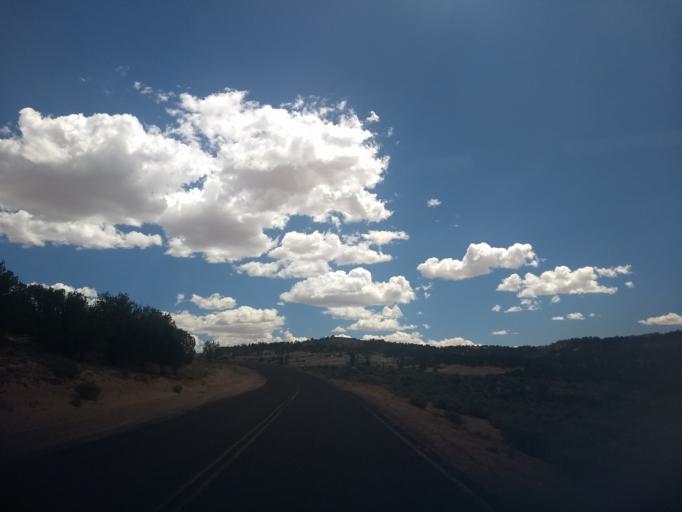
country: US
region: Utah
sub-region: Kane County
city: Kanab
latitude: 37.1255
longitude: -112.6792
